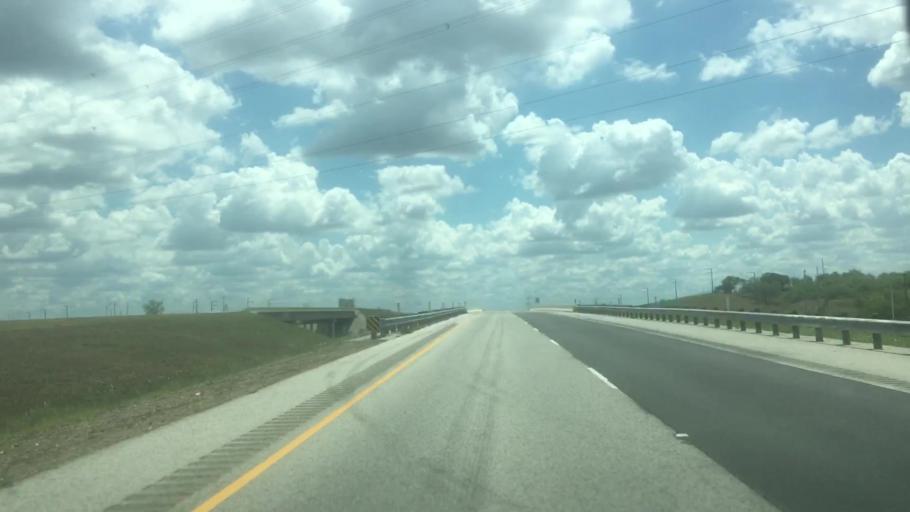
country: US
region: Texas
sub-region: Caldwell County
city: Uhland
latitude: 30.0068
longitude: -97.6876
